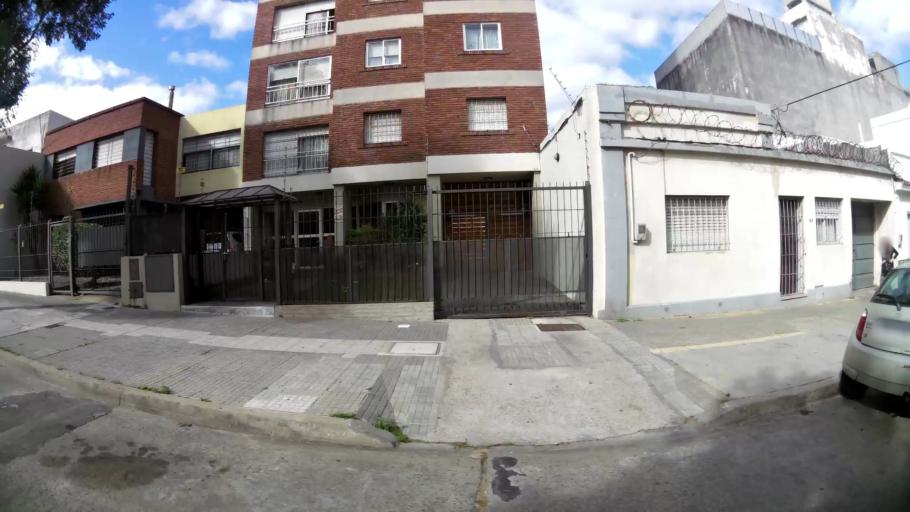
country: UY
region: Montevideo
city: Montevideo
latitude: -34.8863
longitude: -56.1598
